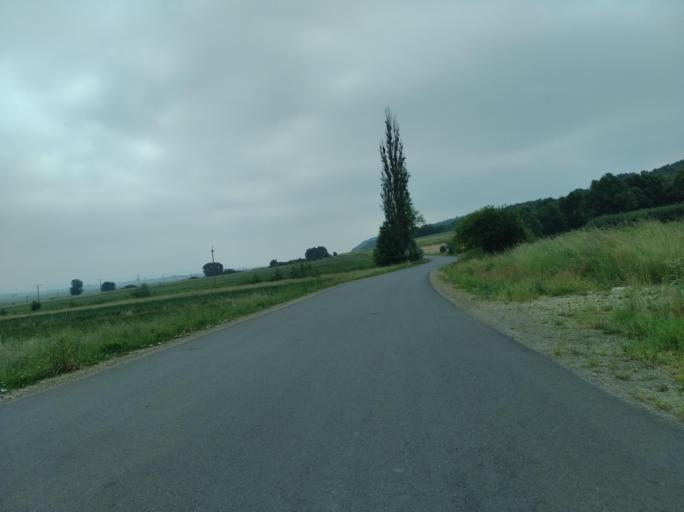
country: PL
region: Subcarpathian Voivodeship
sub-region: Powiat krosnienski
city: Sieniawa
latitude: 49.6009
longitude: 21.9068
